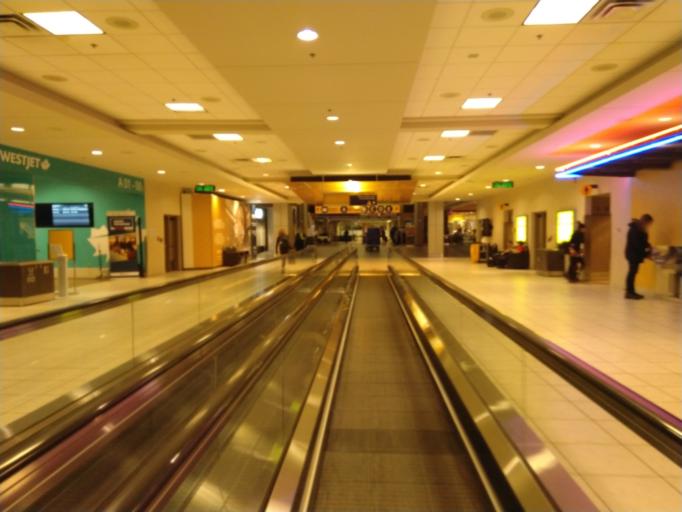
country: CA
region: Alberta
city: Calgary
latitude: 51.1329
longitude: -114.0131
